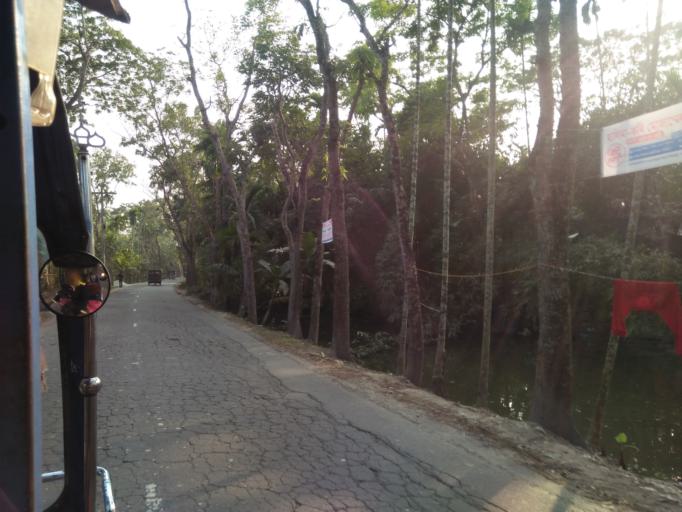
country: BD
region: Barisal
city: Bhola
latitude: 22.7102
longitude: 90.6401
